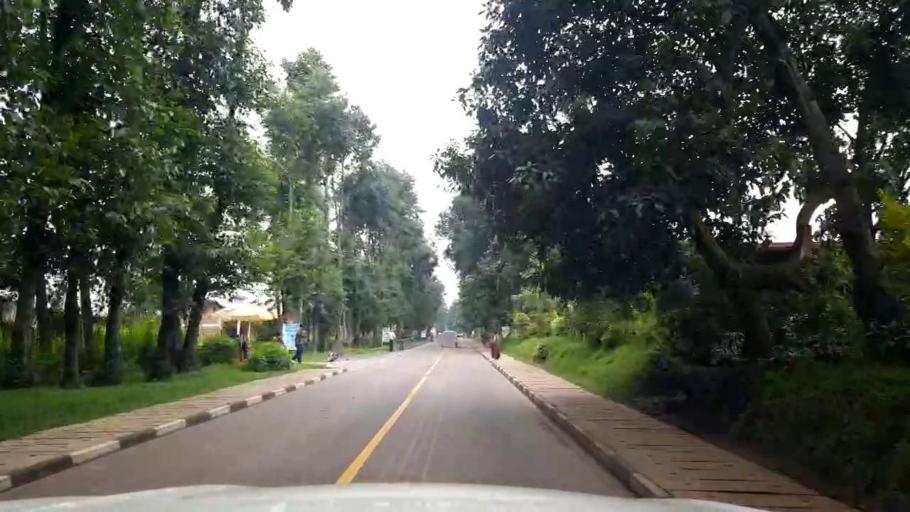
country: RW
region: Northern Province
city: Musanze
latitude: -1.4617
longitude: 29.6138
